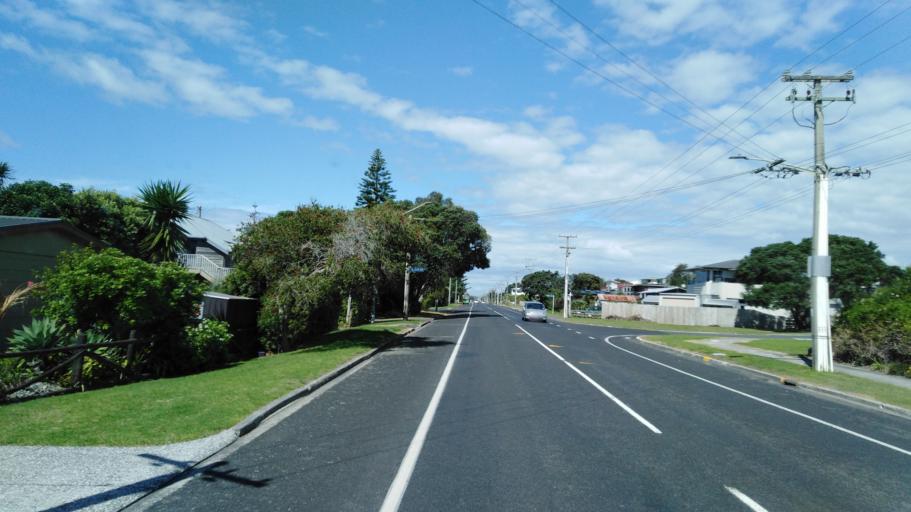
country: NZ
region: Bay of Plenty
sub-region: Western Bay of Plenty District
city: Waihi Beach
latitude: -37.4257
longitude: 175.9554
